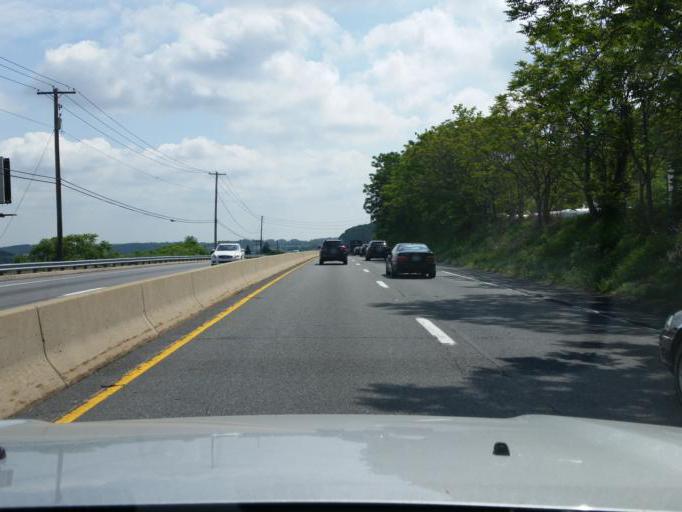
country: US
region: Pennsylvania
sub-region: Dauphin County
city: Rutherford
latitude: 40.2598
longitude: -76.7731
